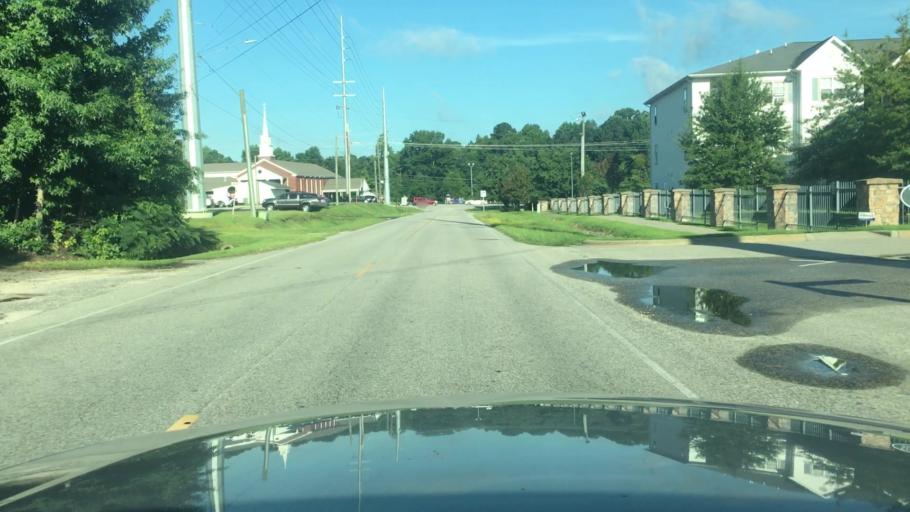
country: US
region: North Carolina
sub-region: Cumberland County
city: Eastover
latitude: 35.1501
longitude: -78.8687
